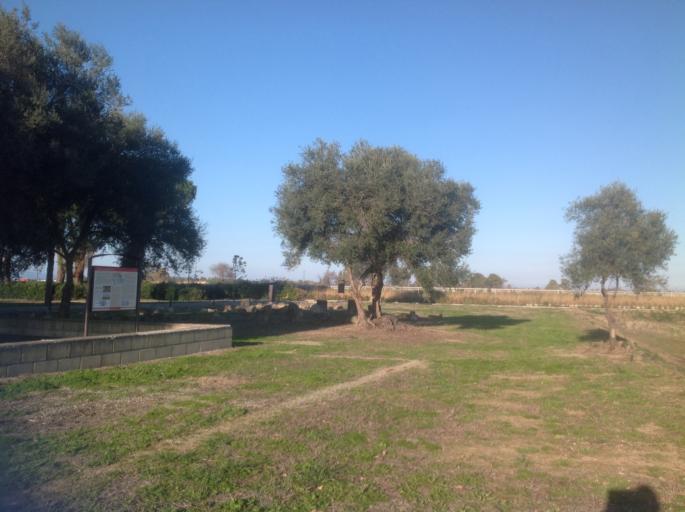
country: IT
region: Calabria
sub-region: Provincia di Cosenza
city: Sibari
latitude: 39.7161
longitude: 16.4919
